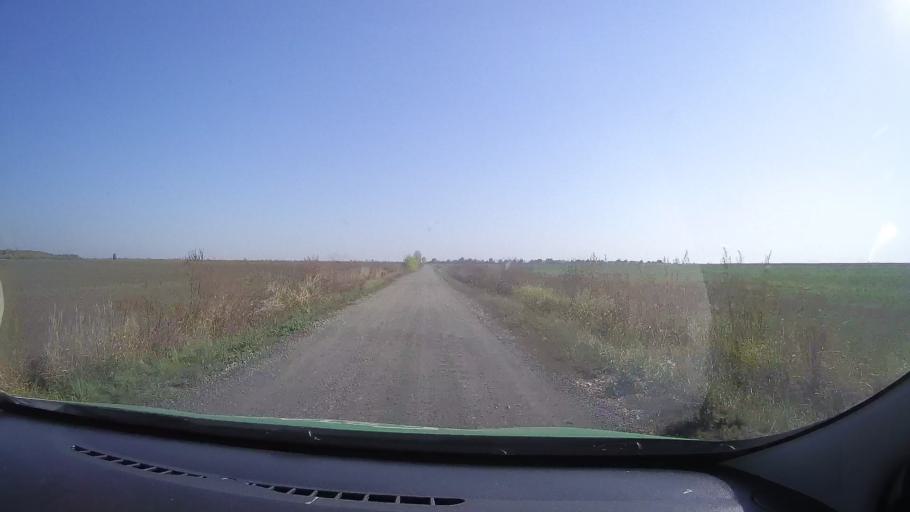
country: RO
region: Satu Mare
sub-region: Comuna Urziceni
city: Urziceni
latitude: 47.7359
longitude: 22.4260
